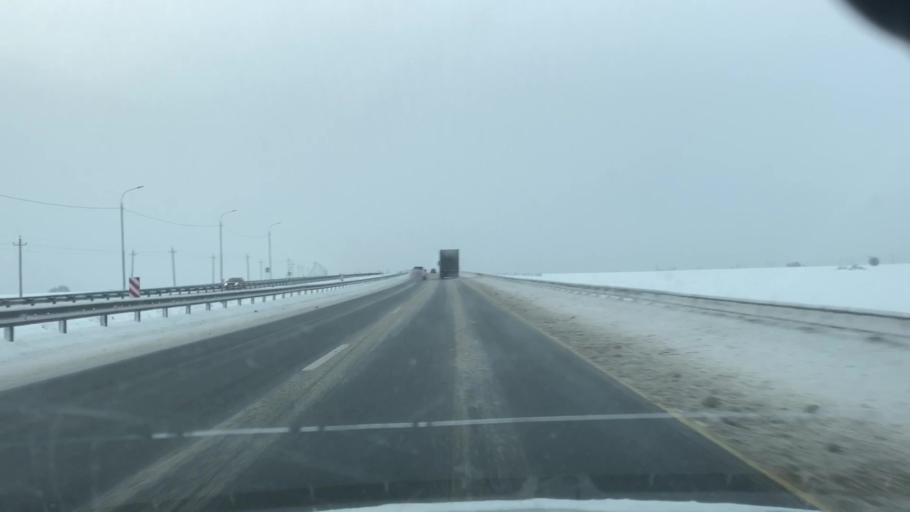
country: RU
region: Moskovskaya
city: Mikhnevo
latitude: 55.1106
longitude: 37.9261
